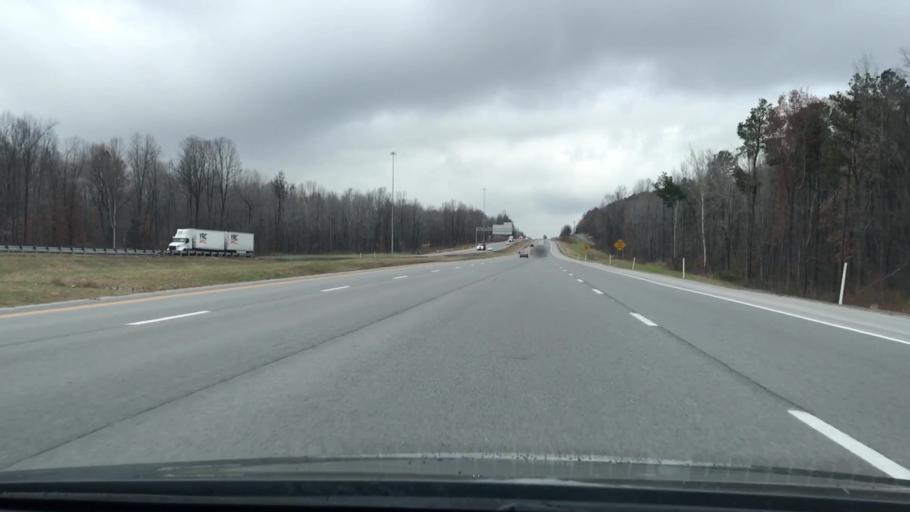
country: US
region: Kentucky
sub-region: Hopkins County
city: Nortonville
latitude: 37.2212
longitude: -87.4431
